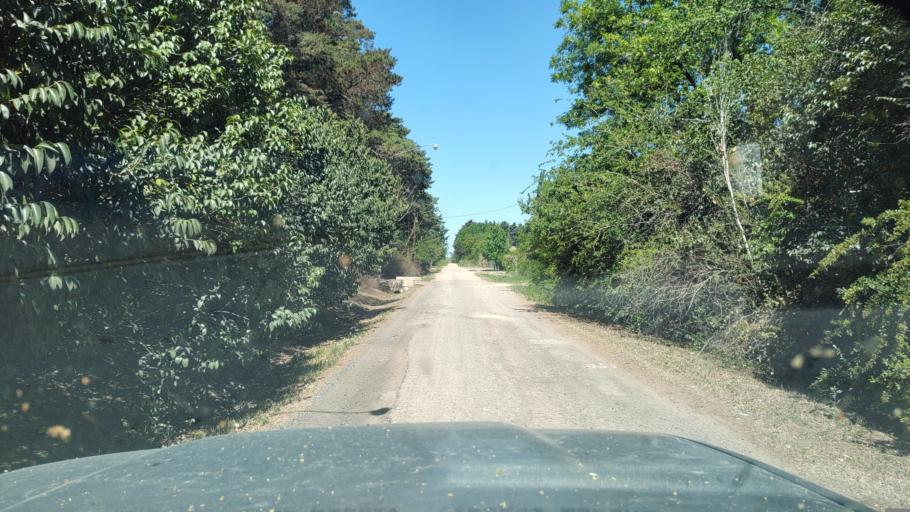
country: AR
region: Buenos Aires
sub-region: Partido de Lujan
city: Lujan
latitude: -34.5979
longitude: -59.1419
